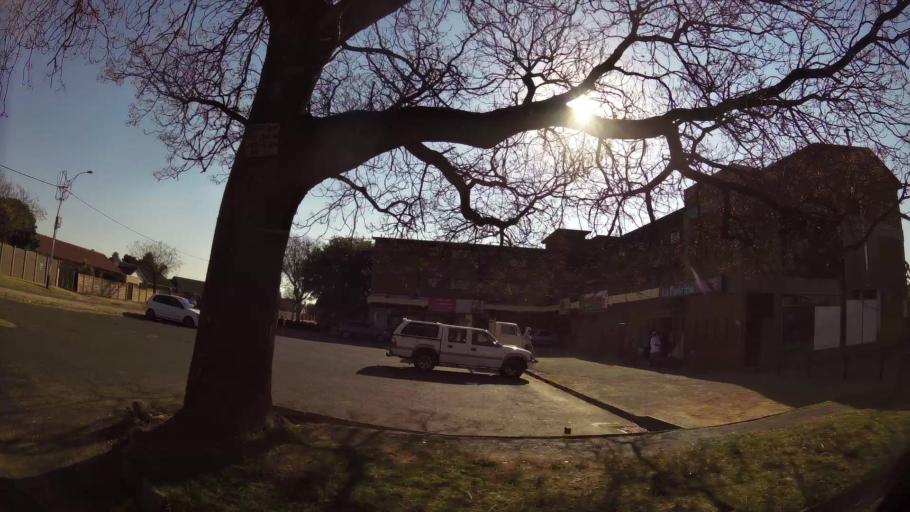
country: ZA
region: Gauteng
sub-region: City of Johannesburg Metropolitan Municipality
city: Johannesburg
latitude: -26.2529
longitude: 28.0121
